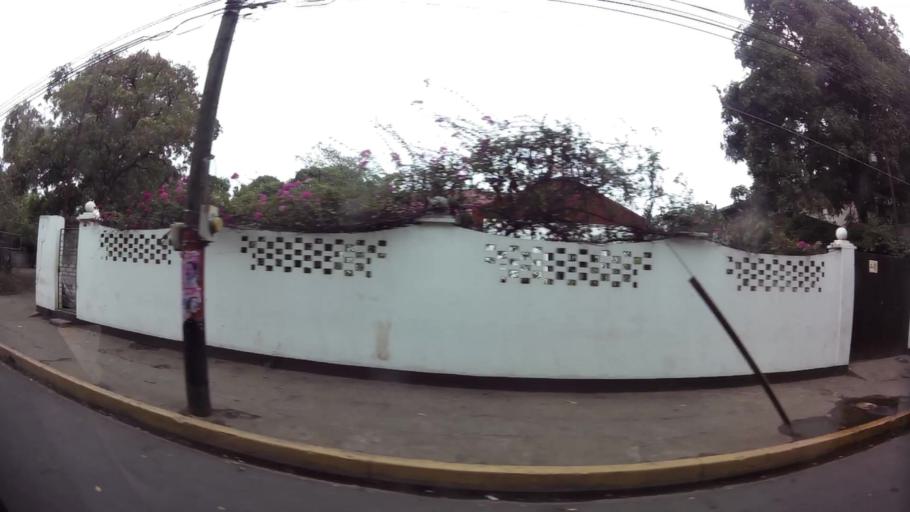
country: NI
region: Leon
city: Leon
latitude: 12.4483
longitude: -86.8716
